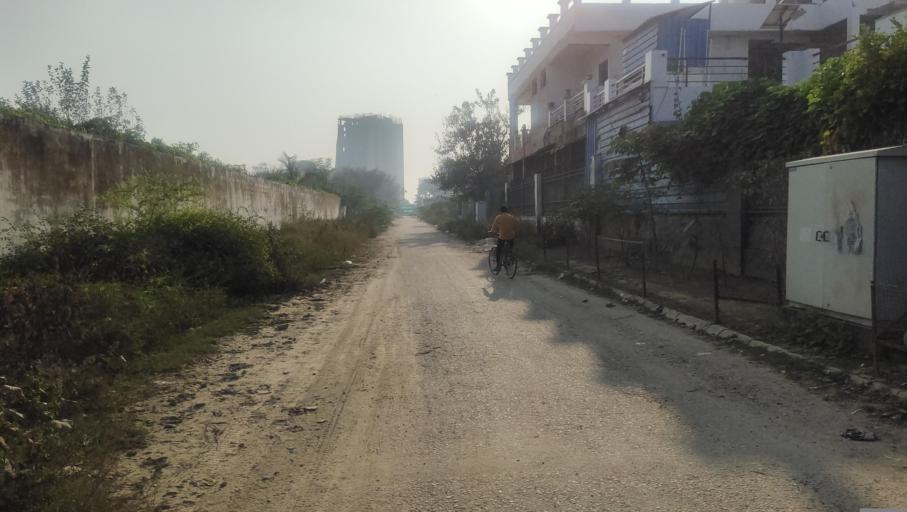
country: IN
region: Uttar Pradesh
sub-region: Lucknow District
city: Goshainganj
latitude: 26.7922
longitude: 81.0127
